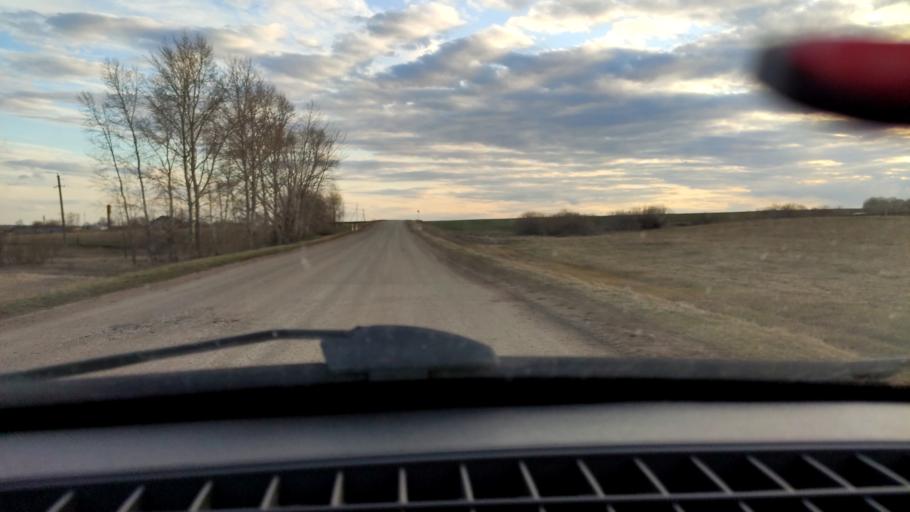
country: RU
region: Bashkortostan
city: Tolbazy
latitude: 54.0037
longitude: 55.6823
